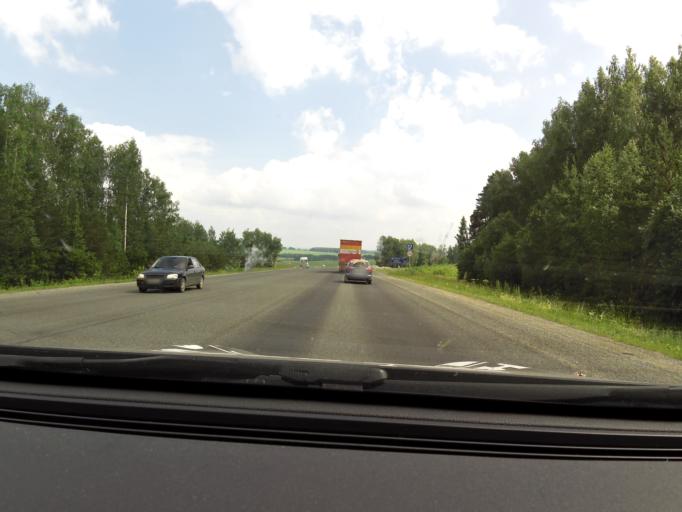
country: RU
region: Sverdlovsk
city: Ufimskiy
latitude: 56.7766
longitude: 57.9919
